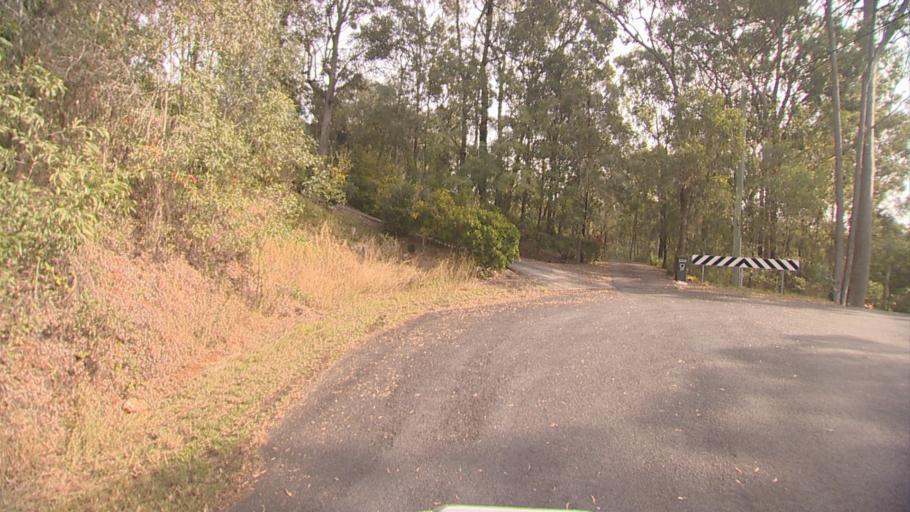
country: AU
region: Queensland
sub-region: Logan
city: Waterford West
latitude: -27.7376
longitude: 153.1433
